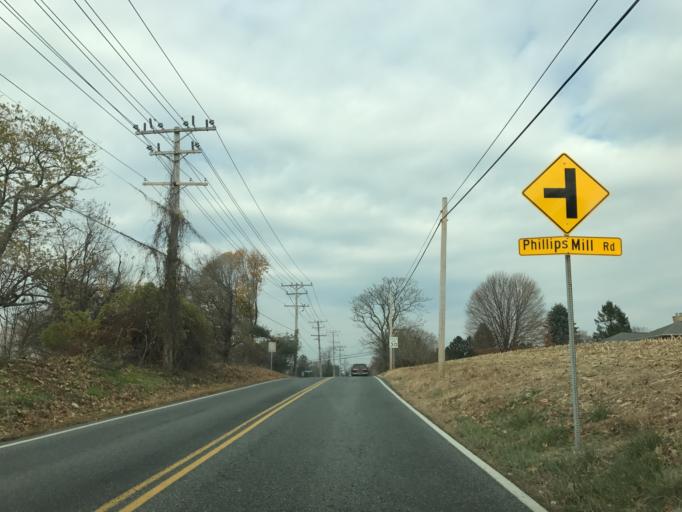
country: US
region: Maryland
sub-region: Harford County
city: Jarrettsville
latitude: 39.5848
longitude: -76.4289
